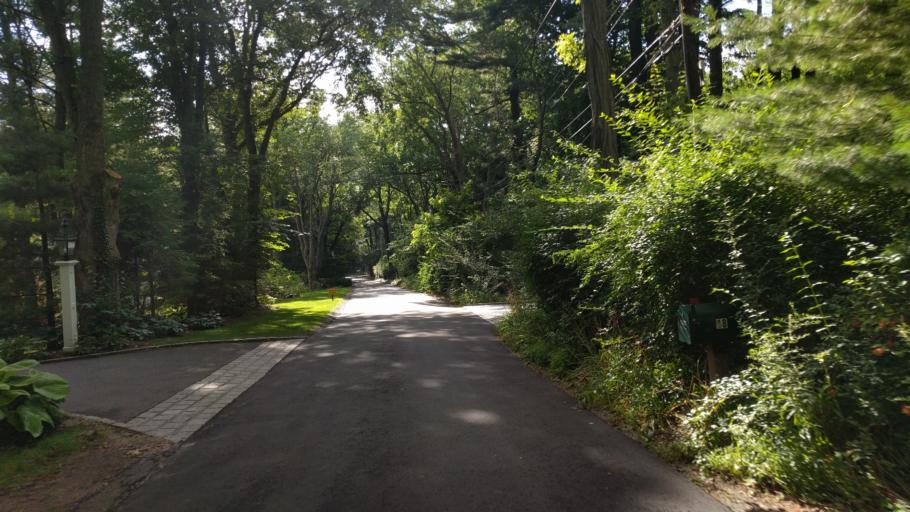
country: US
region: New York
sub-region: Nassau County
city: Oyster Bay Cove
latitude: 40.8692
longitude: -73.4960
